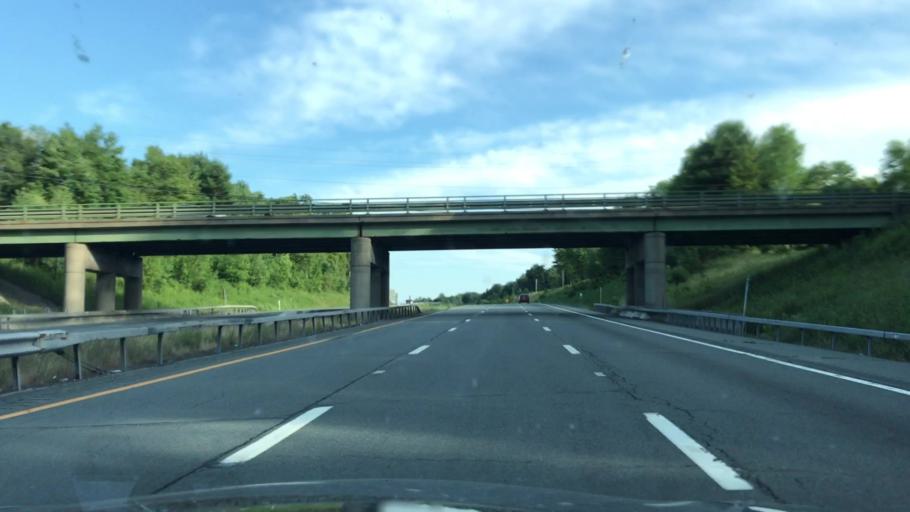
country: US
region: New York
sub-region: Sullivan County
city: Monticello
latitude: 41.6965
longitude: -74.7338
